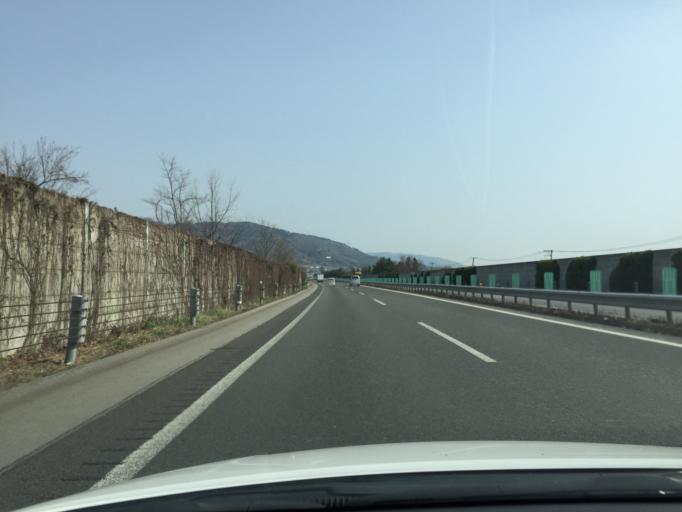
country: JP
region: Fukushima
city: Fukushima-shi
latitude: 37.8100
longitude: 140.4684
